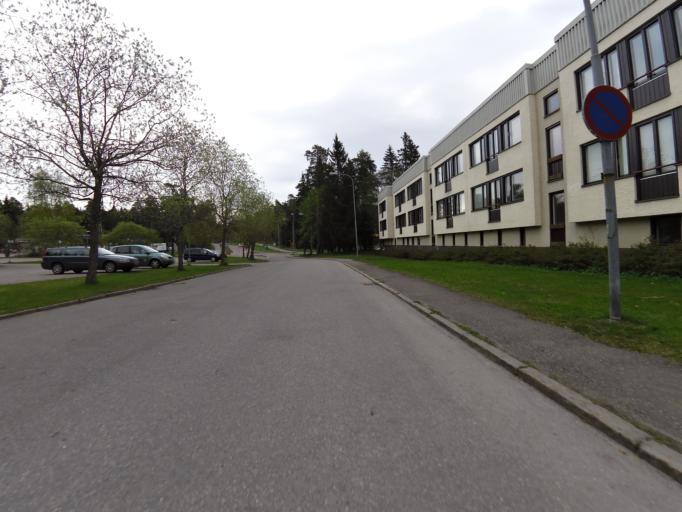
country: SE
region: Gaevleborg
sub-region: Gavle Kommun
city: Gavle
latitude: 60.6883
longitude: 17.1244
